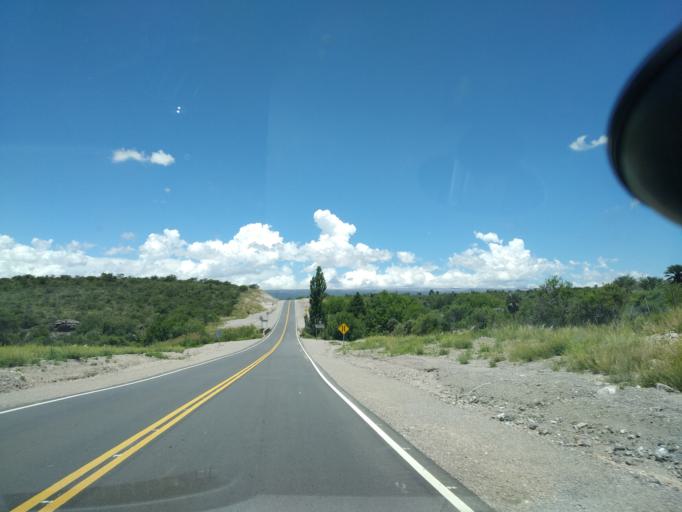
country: AR
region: Cordoba
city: Salsacate
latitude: -31.3460
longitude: -65.0907
